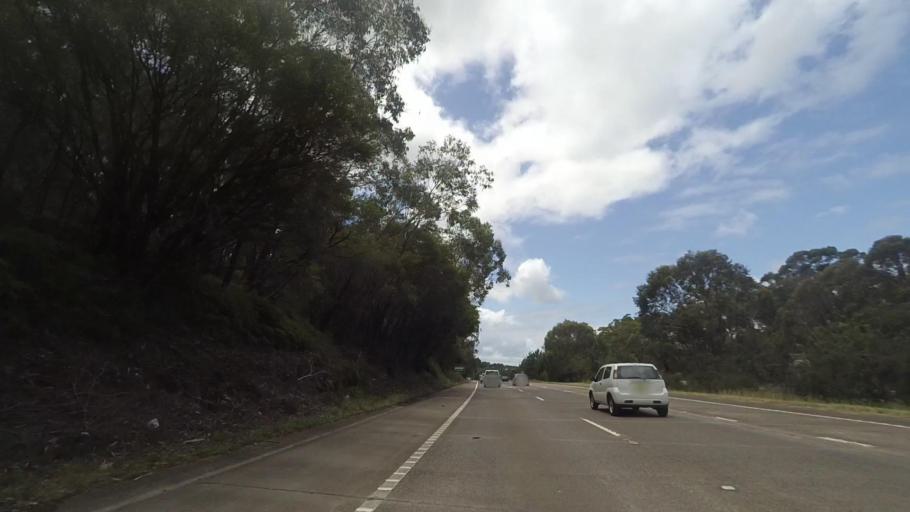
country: AU
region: New South Wales
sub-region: Gosford Shire
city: Narara
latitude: -33.3726
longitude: 151.3069
